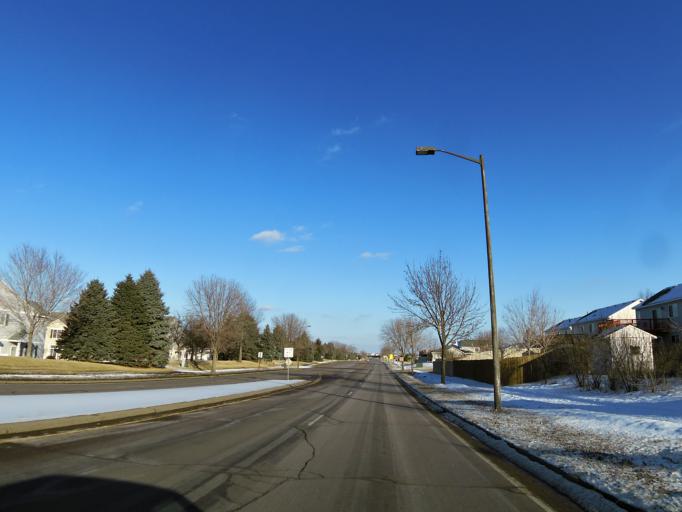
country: US
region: Minnesota
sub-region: Scott County
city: Shakopee
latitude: 44.7736
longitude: -93.4987
